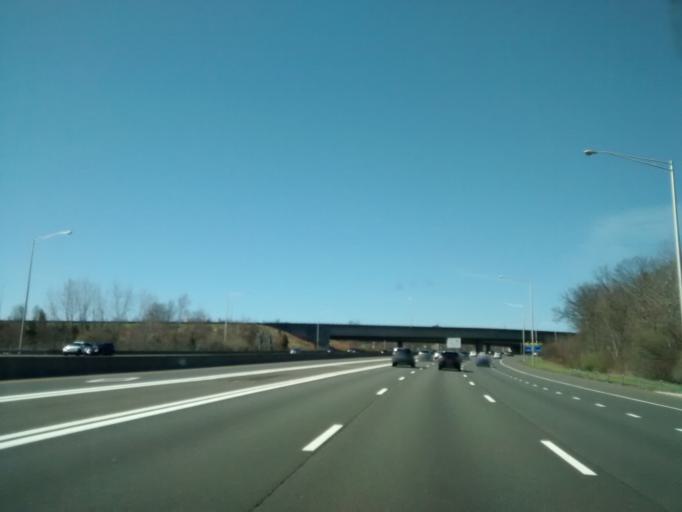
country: US
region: Connecticut
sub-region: Hartford County
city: East Hartford
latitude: 41.7742
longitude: -72.5792
